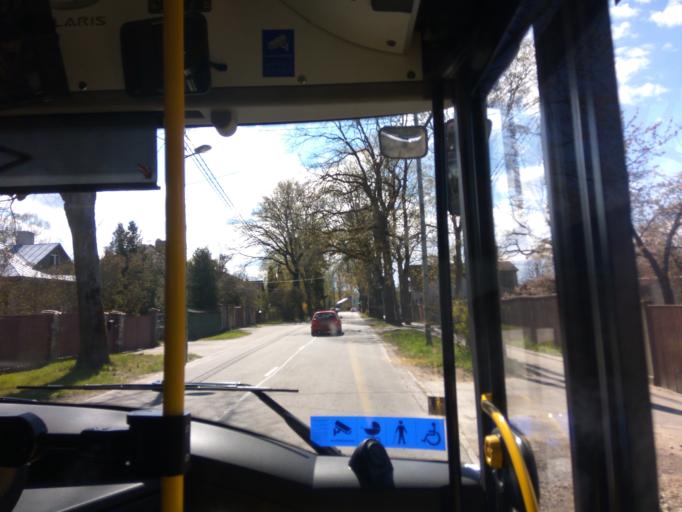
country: LV
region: Marupe
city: Marupe
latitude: 56.9353
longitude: 24.0322
